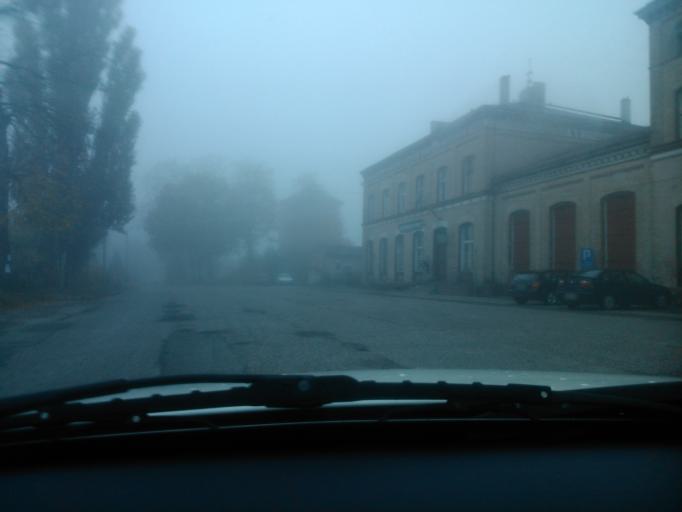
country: PL
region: Kujawsko-Pomorskie
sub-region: Powiat golubsko-dobrzynski
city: Kowalewo Pomorskie
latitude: 53.1642
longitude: 18.8707
